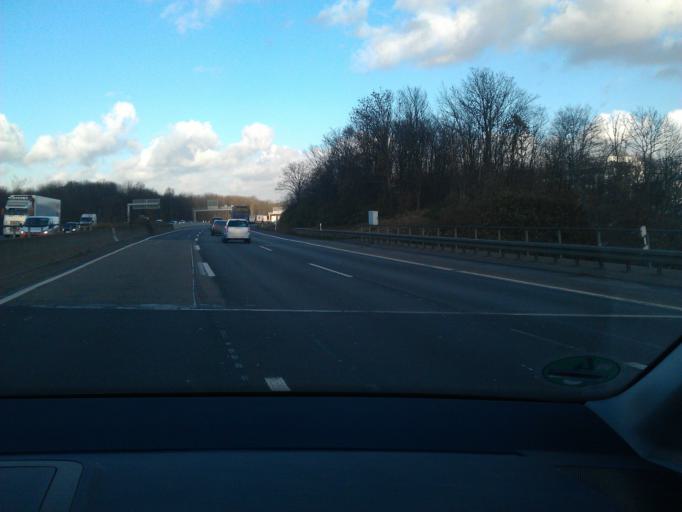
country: DE
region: North Rhine-Westphalia
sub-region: Regierungsbezirk Koln
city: Mengenich
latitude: 50.9775
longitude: 6.8509
